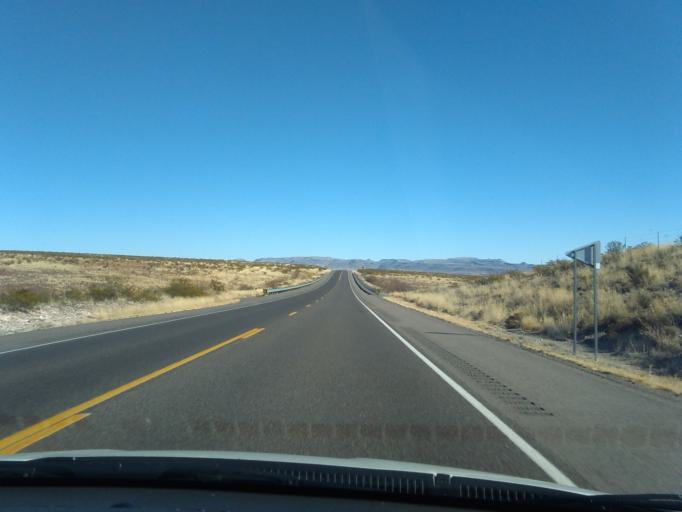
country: US
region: New Mexico
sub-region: Dona Ana County
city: Hatch
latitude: 32.5746
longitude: -107.4160
